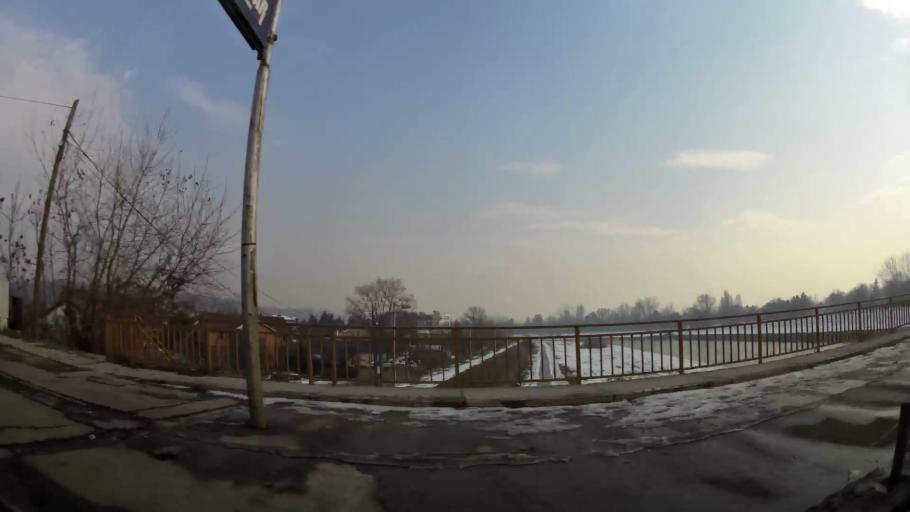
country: MK
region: Karpos
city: Skopje
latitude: 42.0128
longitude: 21.4076
